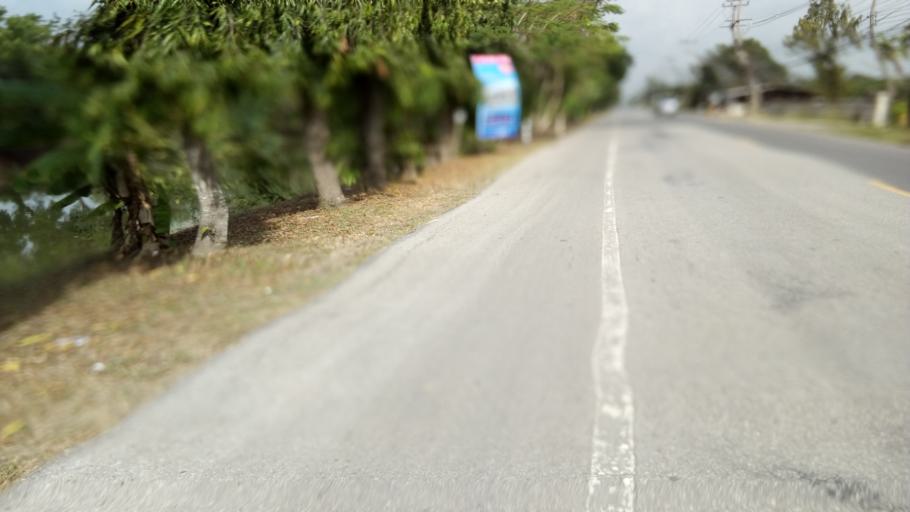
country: TH
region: Pathum Thani
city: Nong Suea
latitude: 14.1443
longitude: 100.8238
